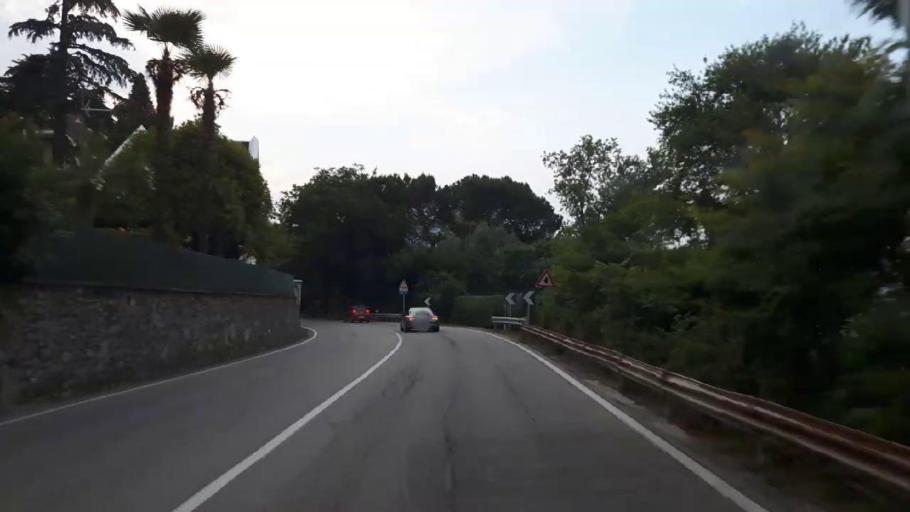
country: IT
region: Piedmont
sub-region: Provincia di Novara
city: Meina
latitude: 45.7830
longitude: 8.5416
